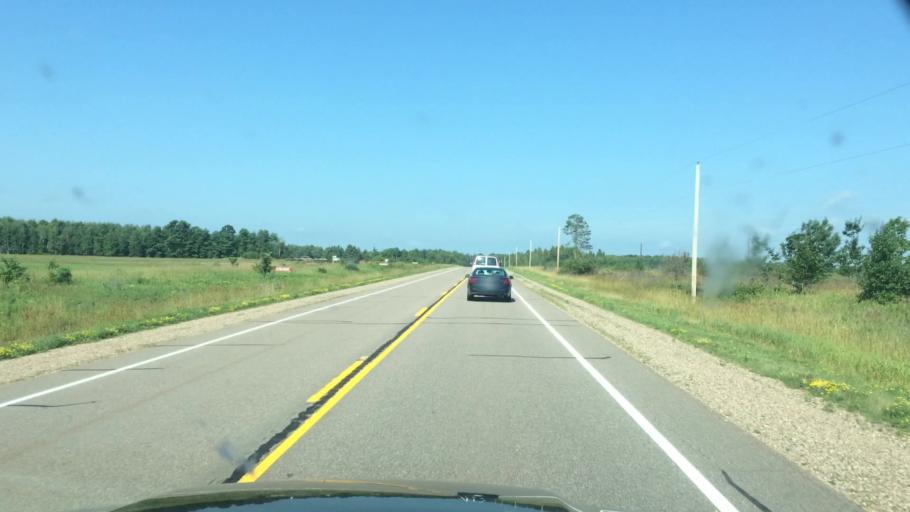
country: US
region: Wisconsin
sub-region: Langlade County
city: Antigo
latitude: 45.1476
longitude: -89.4063
